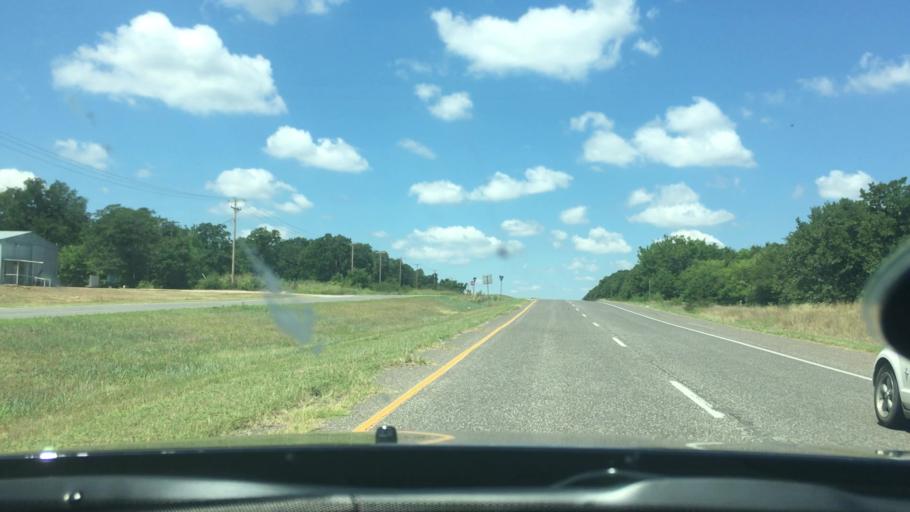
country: US
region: Oklahoma
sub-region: Carter County
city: Lone Grove
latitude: 34.1731
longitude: -97.2899
